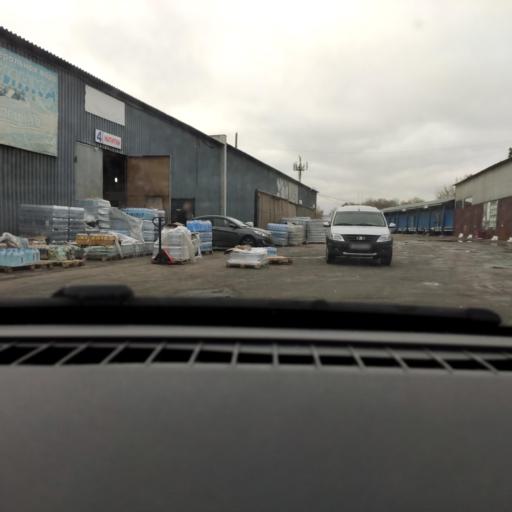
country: RU
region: Voronezj
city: Voronezh
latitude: 51.6583
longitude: 39.2700
